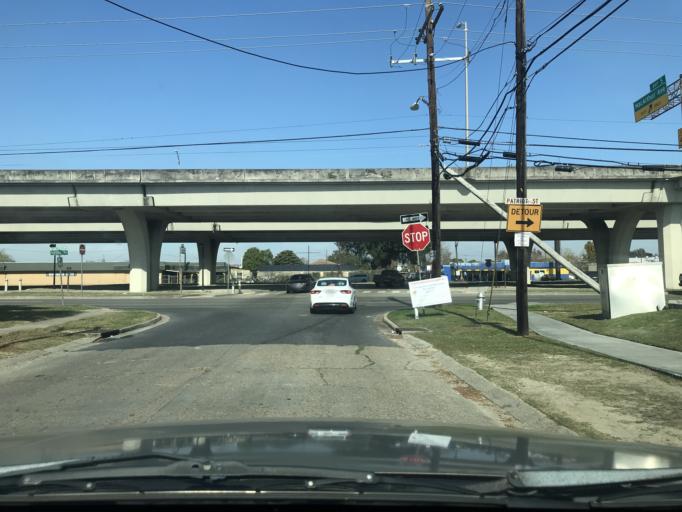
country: US
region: Louisiana
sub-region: Jefferson Parish
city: Marrero
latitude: 29.8952
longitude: -90.0897
